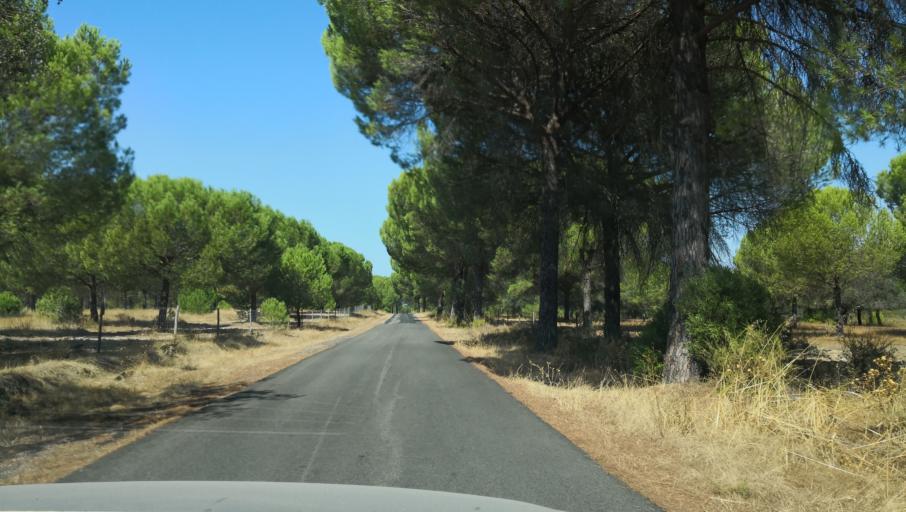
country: PT
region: Setubal
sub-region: Alcacer do Sal
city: Alcacer do Sal
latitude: 38.2587
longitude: -8.3060
